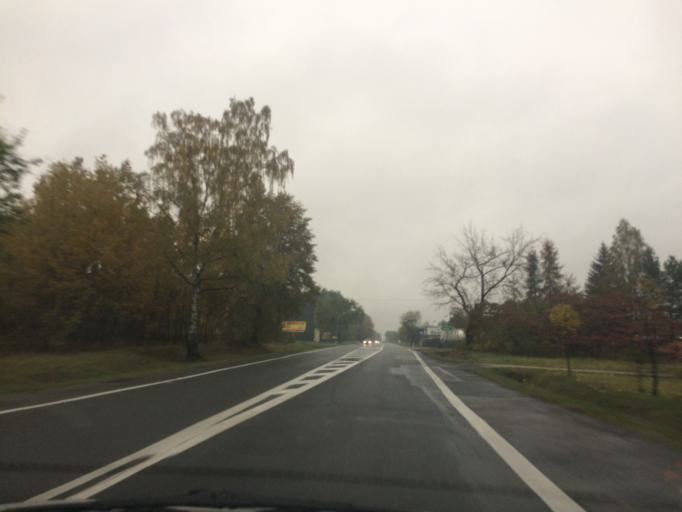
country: PL
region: Masovian Voivodeship
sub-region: Powiat otwocki
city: Celestynow
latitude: 52.0953
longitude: 21.4116
